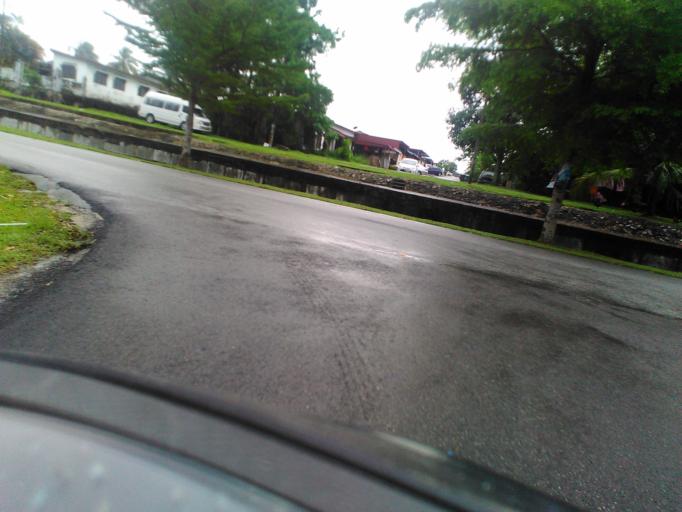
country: MY
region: Kedah
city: Kulim
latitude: 5.3665
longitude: 100.5730
